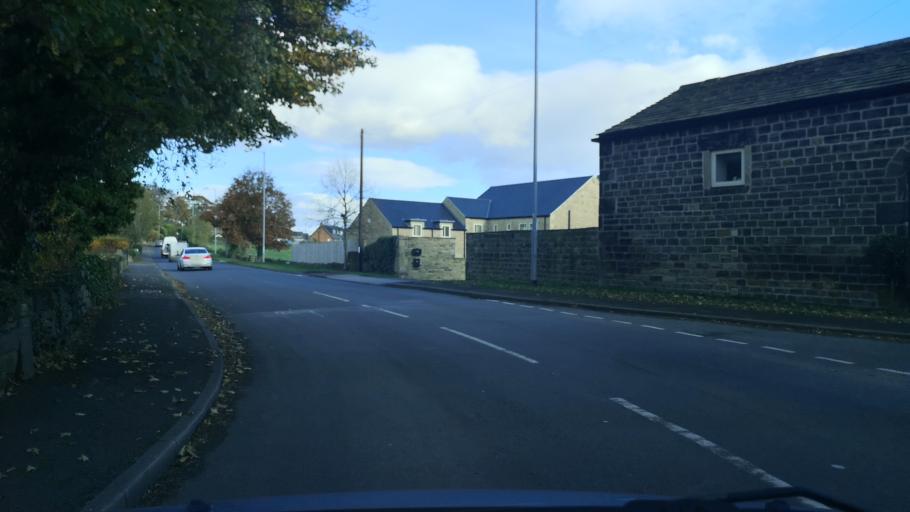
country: GB
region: England
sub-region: City and Borough of Wakefield
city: Horbury
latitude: 53.6199
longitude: -1.5658
